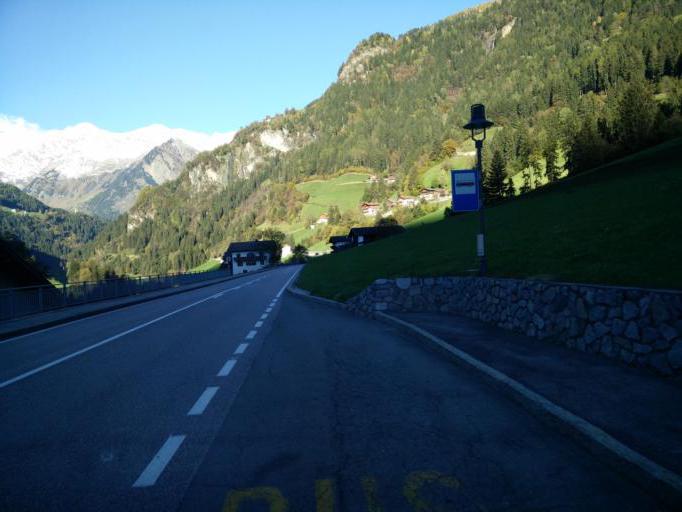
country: IT
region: Trentino-Alto Adige
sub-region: Bolzano
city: San Leonardo in Passiria
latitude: 46.8195
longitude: 11.2258
